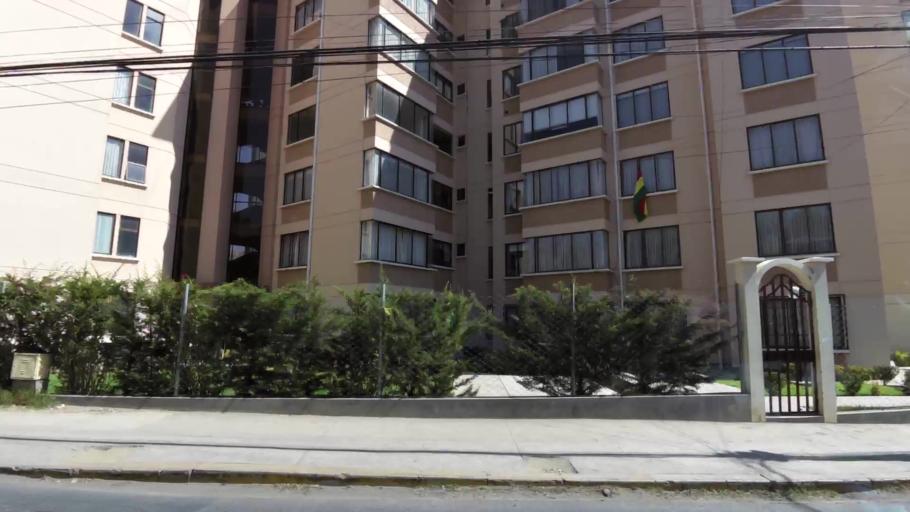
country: BO
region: La Paz
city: La Paz
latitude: -16.5432
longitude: -68.0708
